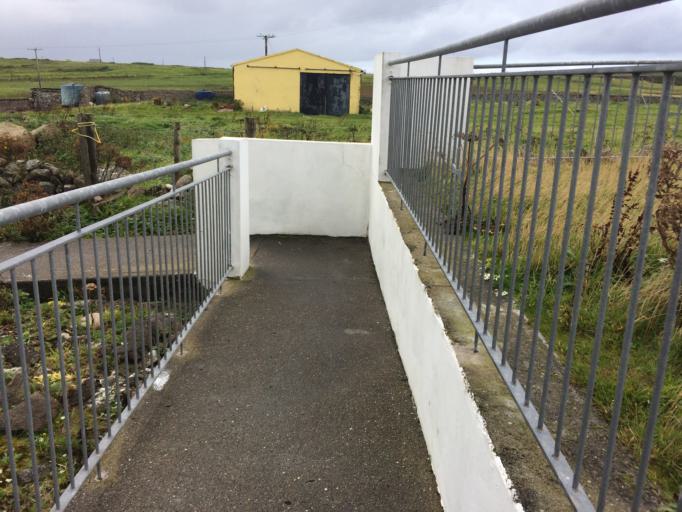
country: IE
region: Ulster
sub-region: County Donegal
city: Derrybeg
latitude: 55.2657
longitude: -8.2255
